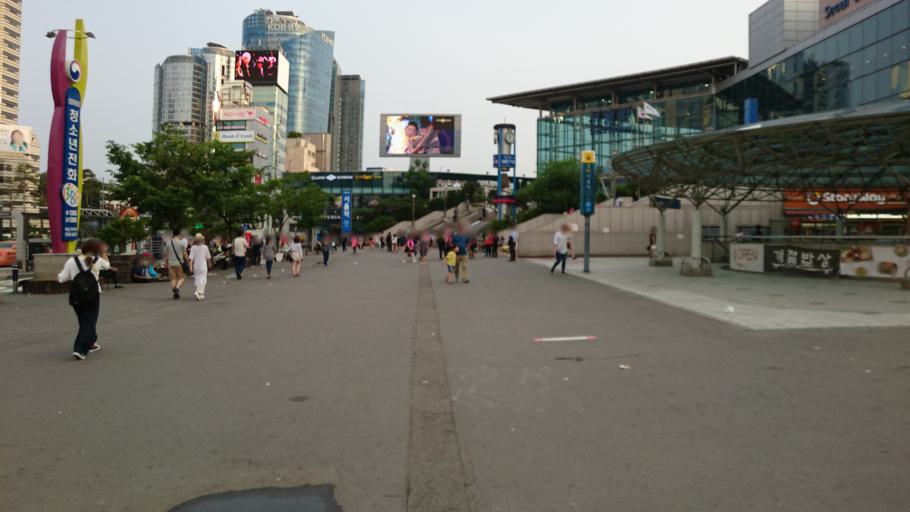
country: KR
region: Seoul
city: Seoul
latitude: 37.5552
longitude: 126.9719
